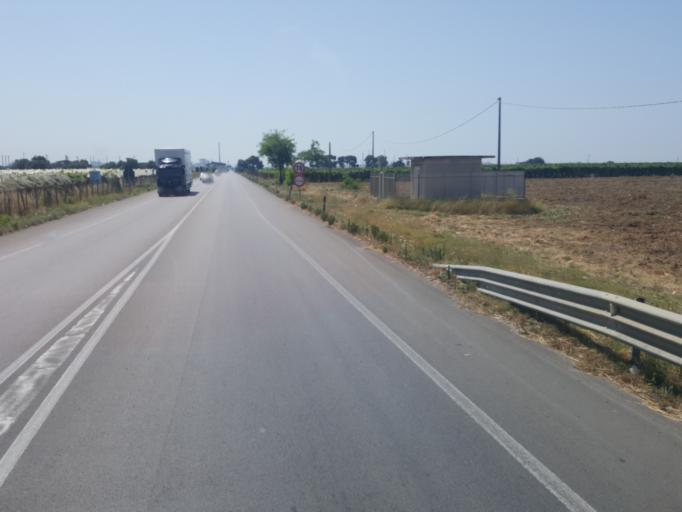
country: IT
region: Apulia
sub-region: Provincia di Taranto
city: Statte
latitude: 40.5347
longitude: 17.1618
